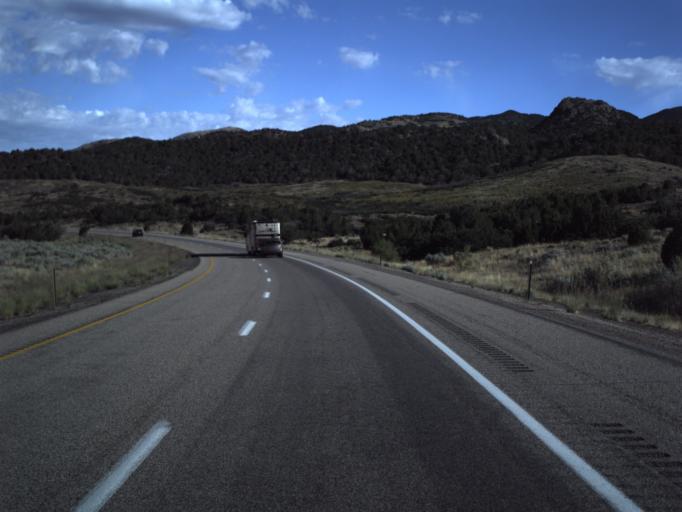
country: US
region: Utah
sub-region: Beaver County
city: Beaver
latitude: 38.6050
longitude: -112.5066
